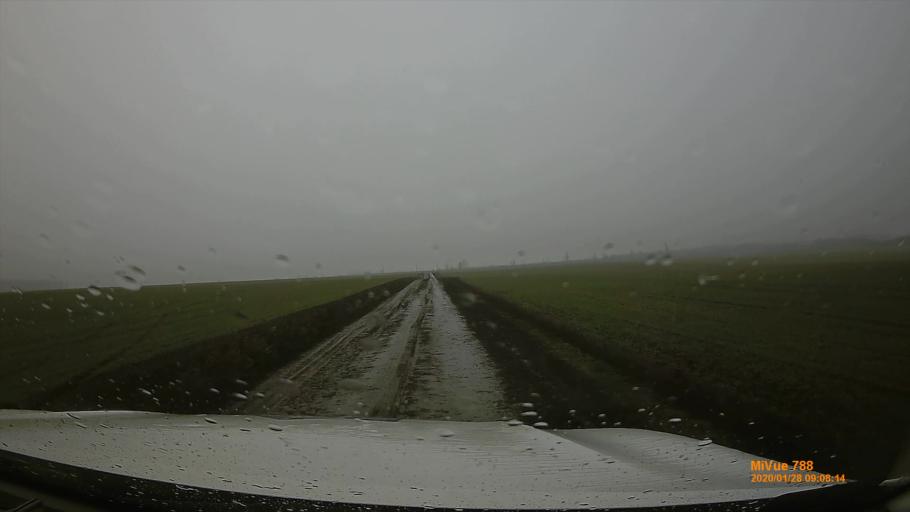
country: HU
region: Pest
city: Pilis
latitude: 47.3135
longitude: 19.5437
